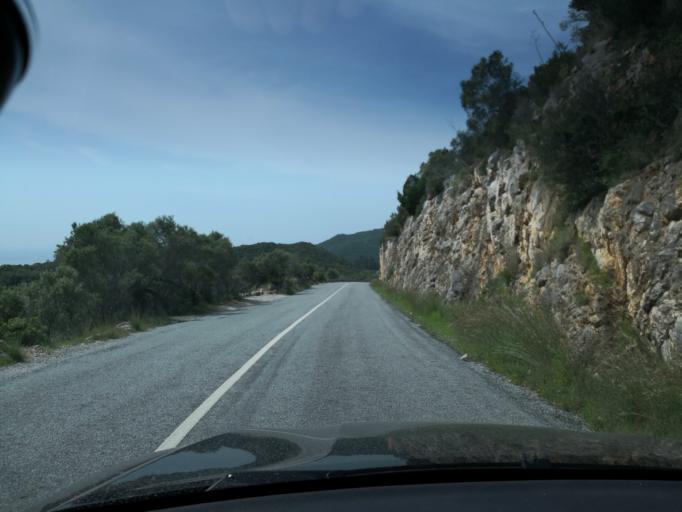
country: PT
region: Setubal
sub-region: Palmela
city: Quinta do Anjo
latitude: 38.4764
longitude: -8.9867
